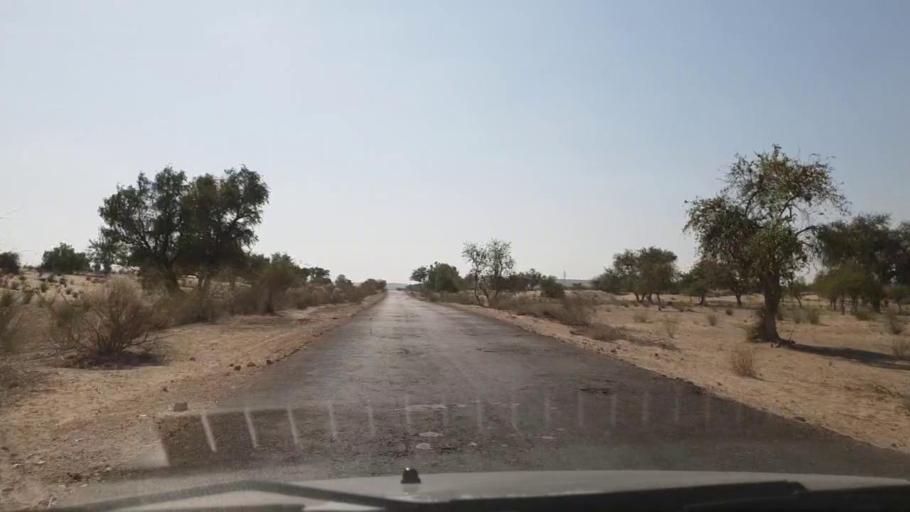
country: PK
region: Sindh
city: Mithi
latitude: 24.6601
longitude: 69.7568
